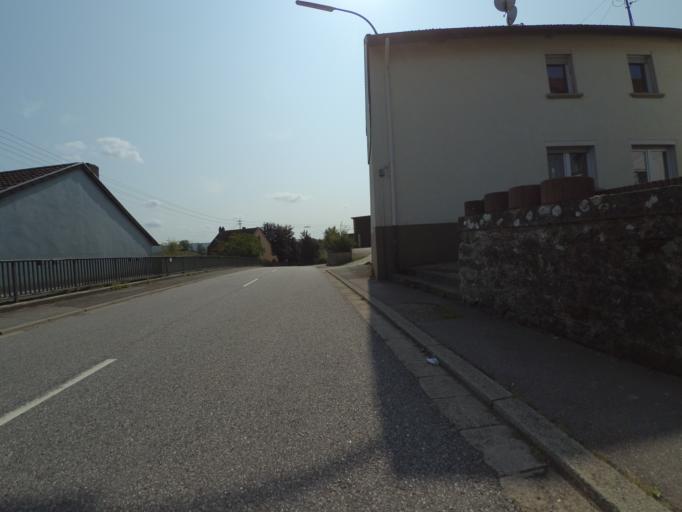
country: DE
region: Saarland
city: Mettlach
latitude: 49.4694
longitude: 6.5893
